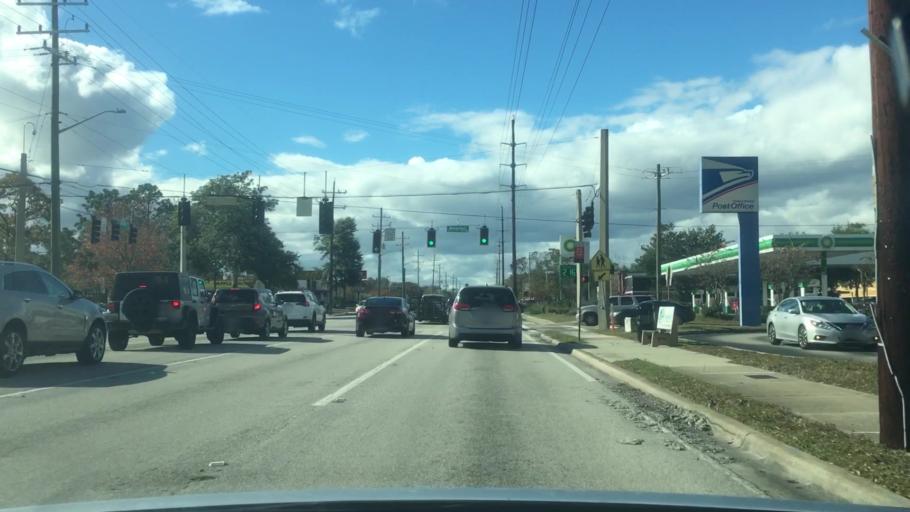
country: US
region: Florida
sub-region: Duval County
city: Jacksonville
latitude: 30.3523
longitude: -81.5683
